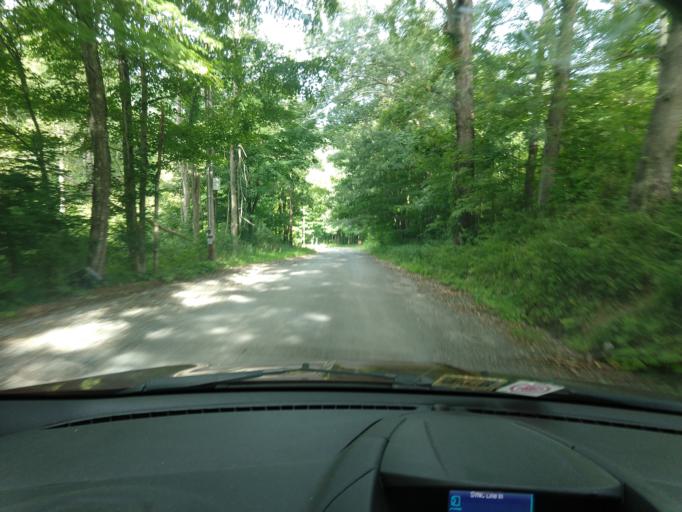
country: US
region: West Virginia
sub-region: Nicholas County
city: Richwood
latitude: 38.1559
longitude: -80.6890
